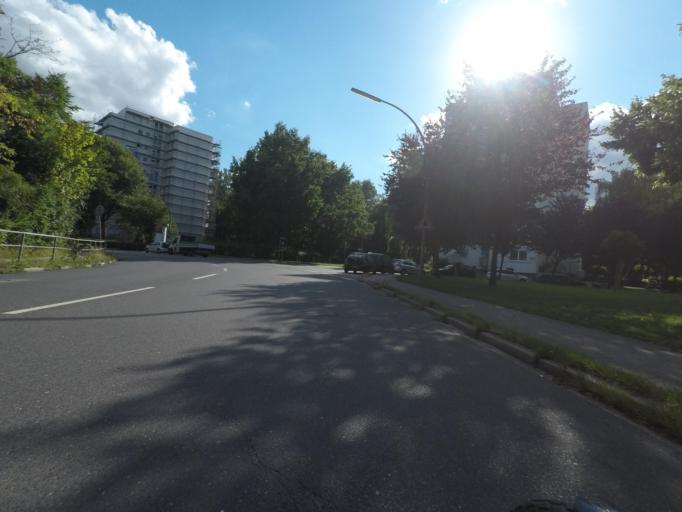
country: DE
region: Hamburg
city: Steilshoop
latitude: 53.6042
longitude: 10.0780
